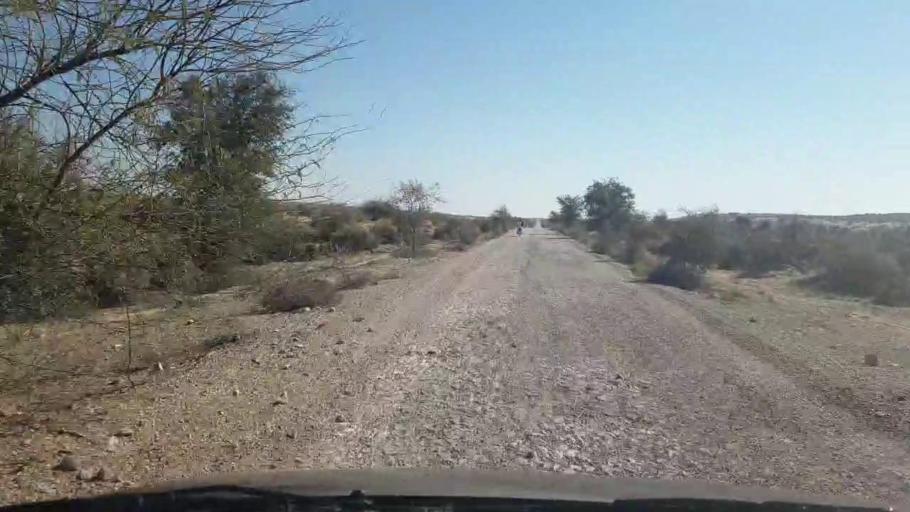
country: PK
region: Sindh
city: Bozdar
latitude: 27.0318
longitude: 68.7026
